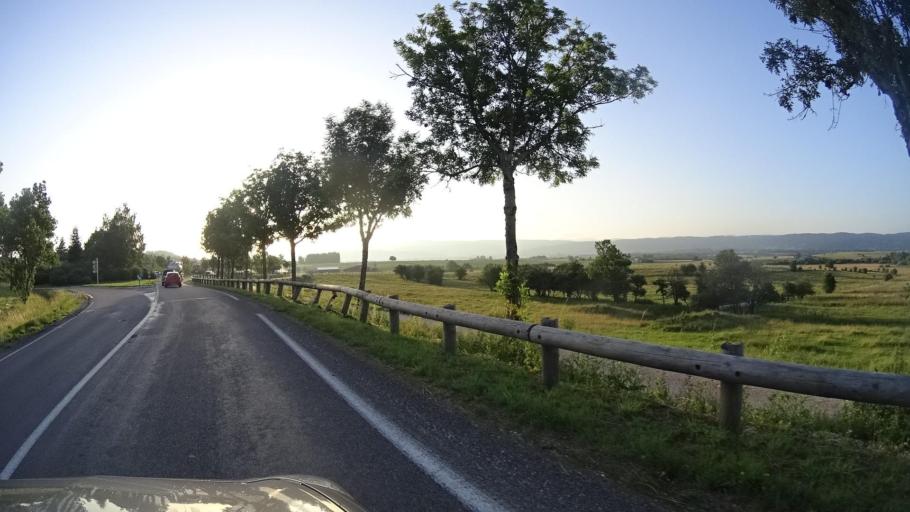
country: FR
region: Franche-Comte
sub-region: Departement du Doubs
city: Doubs
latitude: 46.9089
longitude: 6.2667
